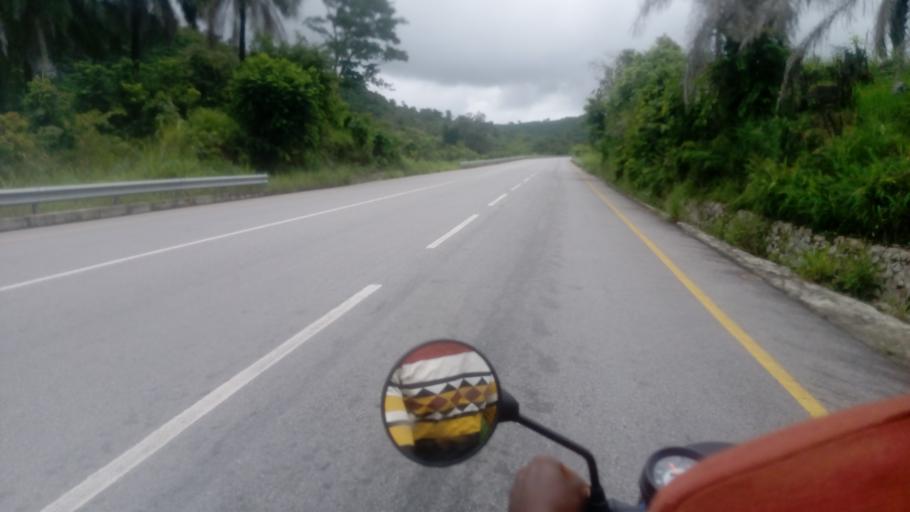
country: SL
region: Northern Province
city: Masaka
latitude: 8.6620
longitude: -11.7932
